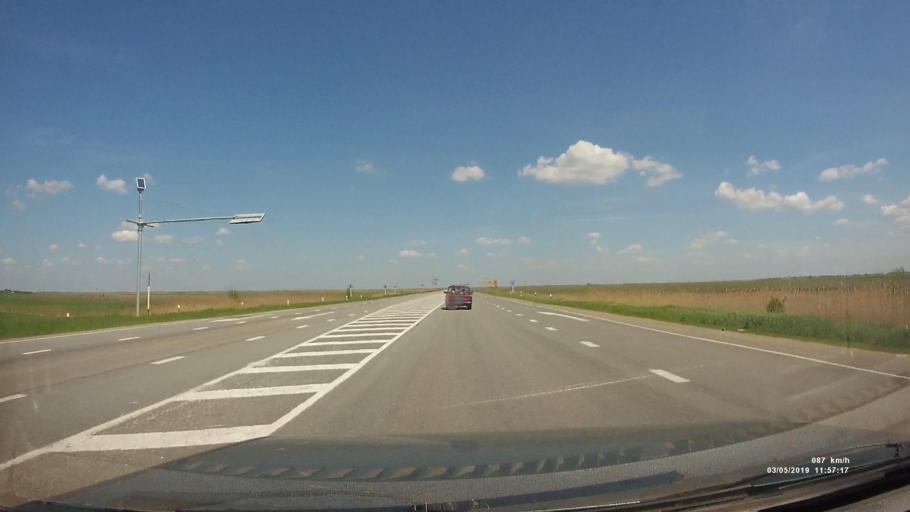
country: RU
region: Rostov
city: Bagayevskaya
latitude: 47.2047
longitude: 40.3084
